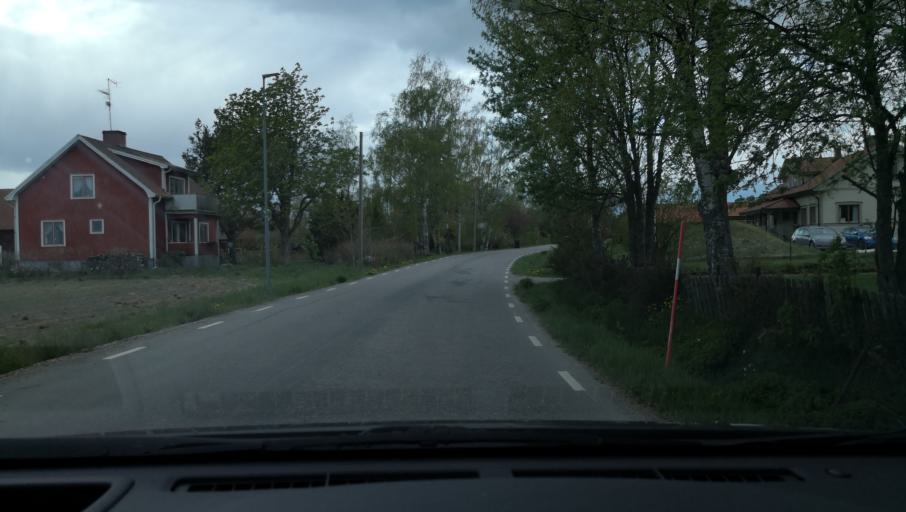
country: SE
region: Dalarna
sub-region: Avesta Kommun
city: Avesta
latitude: 60.0199
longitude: 16.2843
